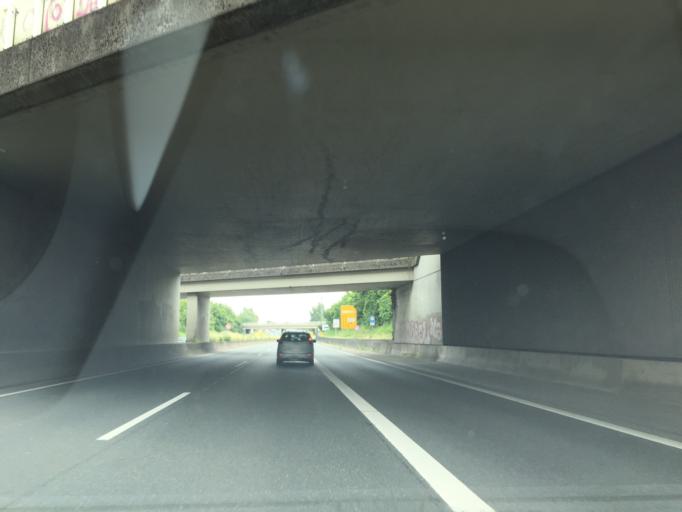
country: DE
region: North Rhine-Westphalia
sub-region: Regierungsbezirk Munster
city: Muenster
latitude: 51.9372
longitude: 7.6290
